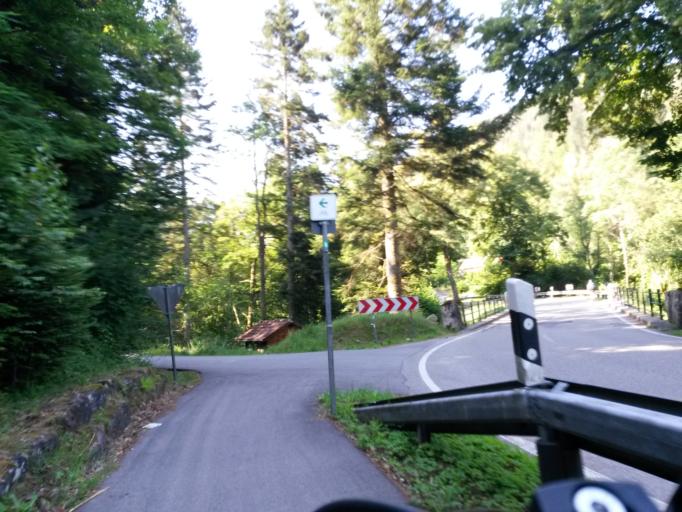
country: DE
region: Baden-Wuerttemberg
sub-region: Karlsruhe Region
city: Bad Wildbad
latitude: 48.7172
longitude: 8.5425
